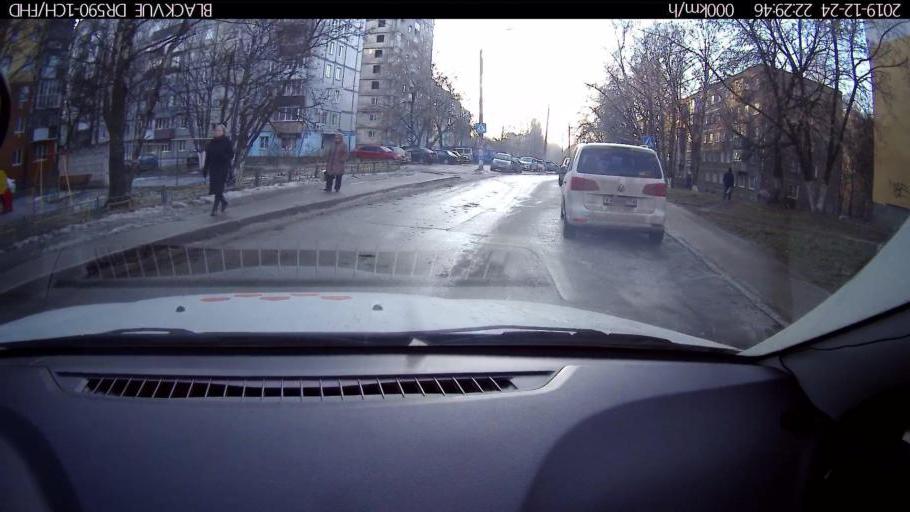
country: RU
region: Nizjnij Novgorod
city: Nizhniy Novgorod
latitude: 56.2365
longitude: 43.9606
